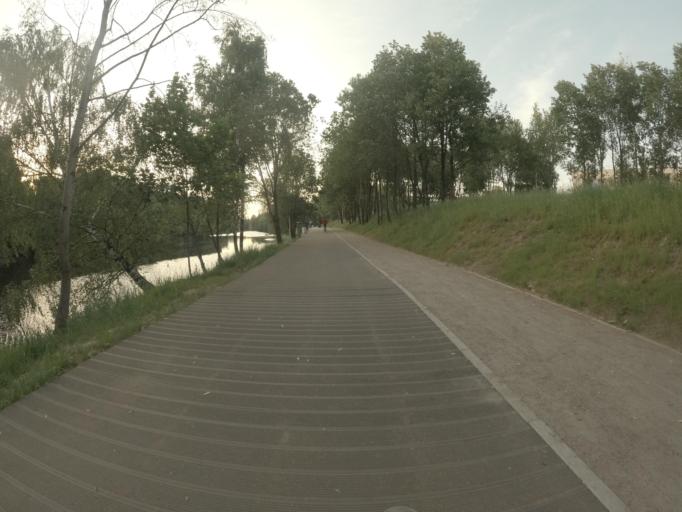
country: RU
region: St.-Petersburg
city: Krasnogvargeisky
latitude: 59.9444
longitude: 30.4570
